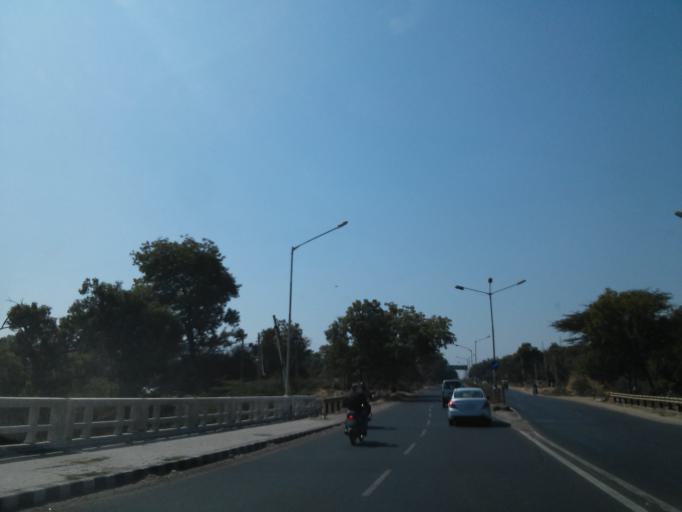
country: IN
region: Gujarat
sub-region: Gandhinagar
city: Ghandinagar
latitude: 23.2445
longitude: 72.6830
